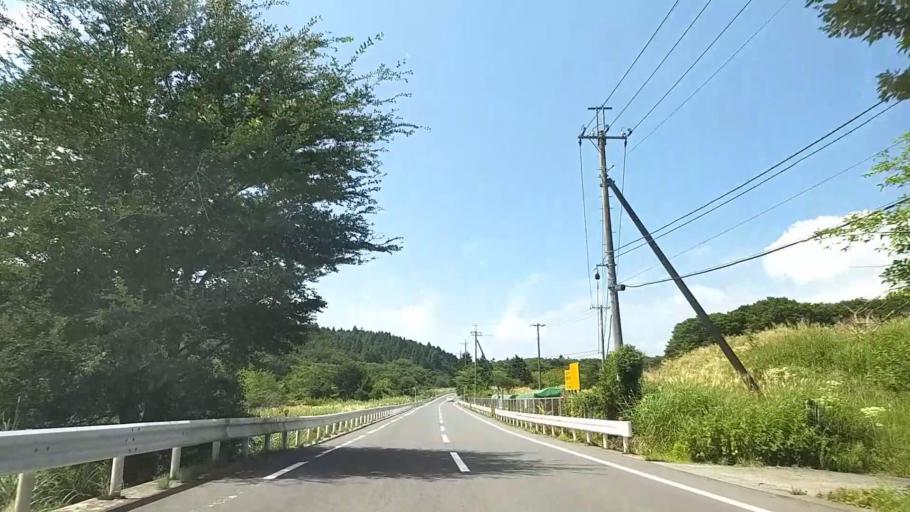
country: JP
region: Shizuoka
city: Gotemba
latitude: 35.2565
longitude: 138.7999
